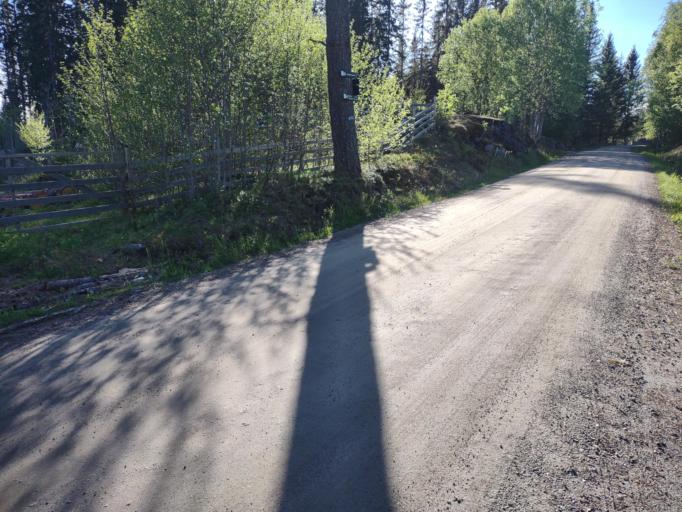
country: NO
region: Oppland
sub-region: Gran
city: Jaren
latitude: 60.4678
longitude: 10.5217
